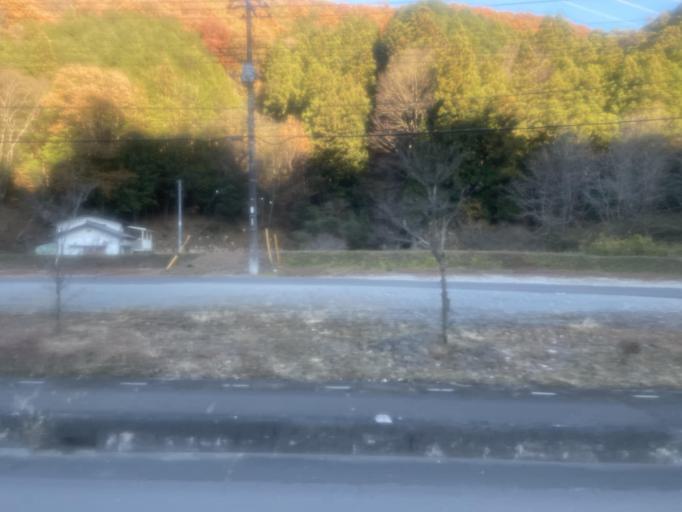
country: JP
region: Saitama
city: Yorii
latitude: 36.0769
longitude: 139.1781
